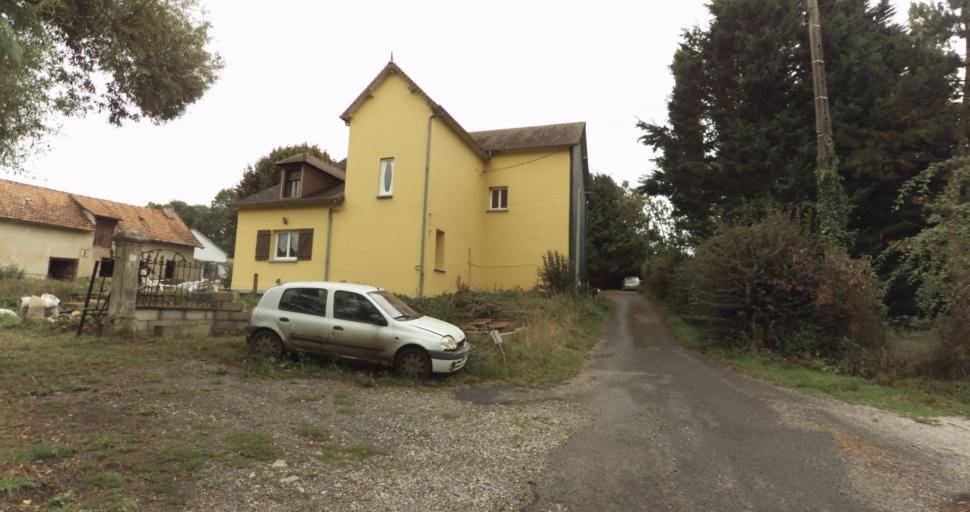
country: FR
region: Lower Normandy
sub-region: Departement de l'Orne
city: Sainte-Gauburge-Sainte-Colombe
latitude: 48.7306
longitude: 0.4816
